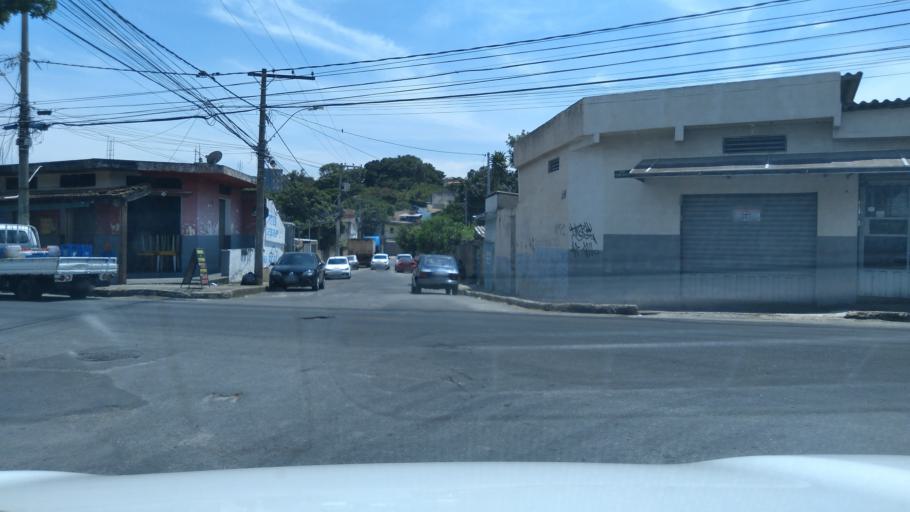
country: BR
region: Minas Gerais
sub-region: Contagem
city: Contagem
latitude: -19.8993
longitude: -44.0107
